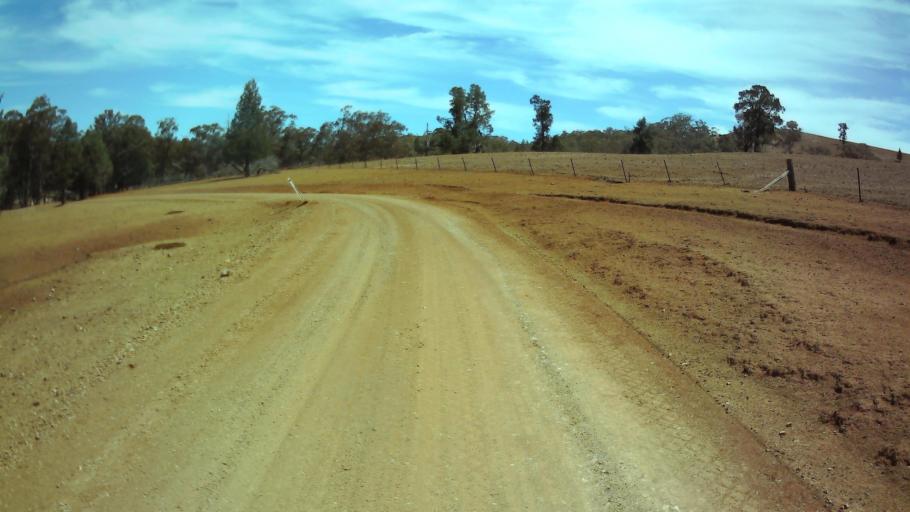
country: AU
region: New South Wales
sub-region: Weddin
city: Grenfell
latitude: -33.7965
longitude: 148.1600
